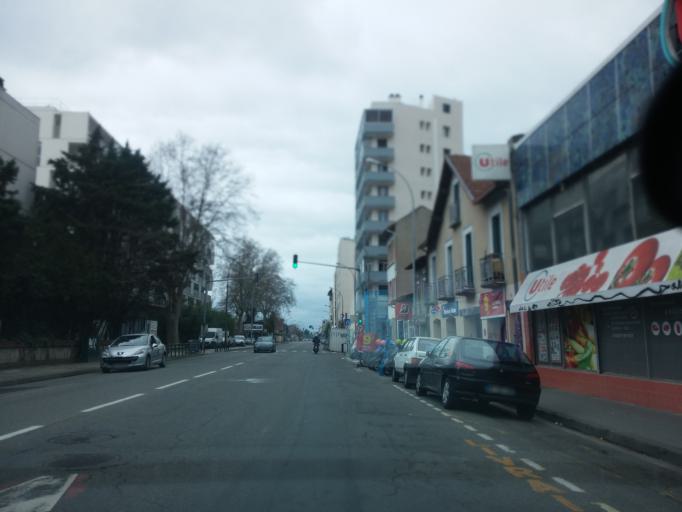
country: FR
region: Midi-Pyrenees
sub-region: Departement de la Haute-Garonne
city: Toulouse
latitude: 43.5984
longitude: 1.4187
